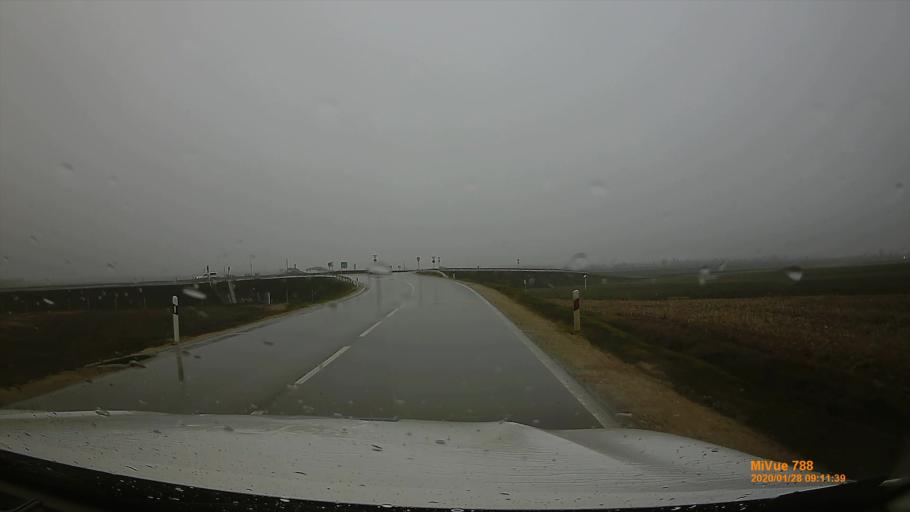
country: HU
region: Pest
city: Pilis
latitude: 47.3092
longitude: 19.5532
